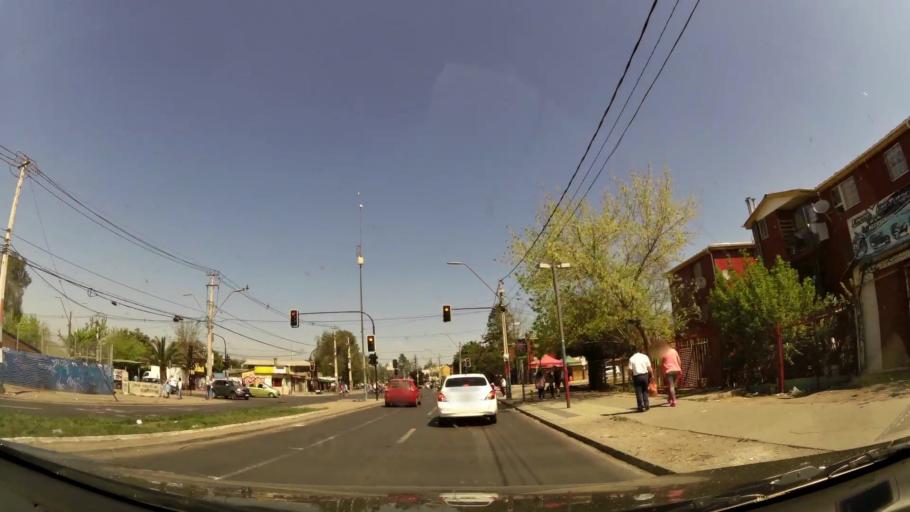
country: CL
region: Santiago Metropolitan
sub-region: Provincia de Santiago
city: Lo Prado
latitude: -33.4053
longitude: -70.7455
